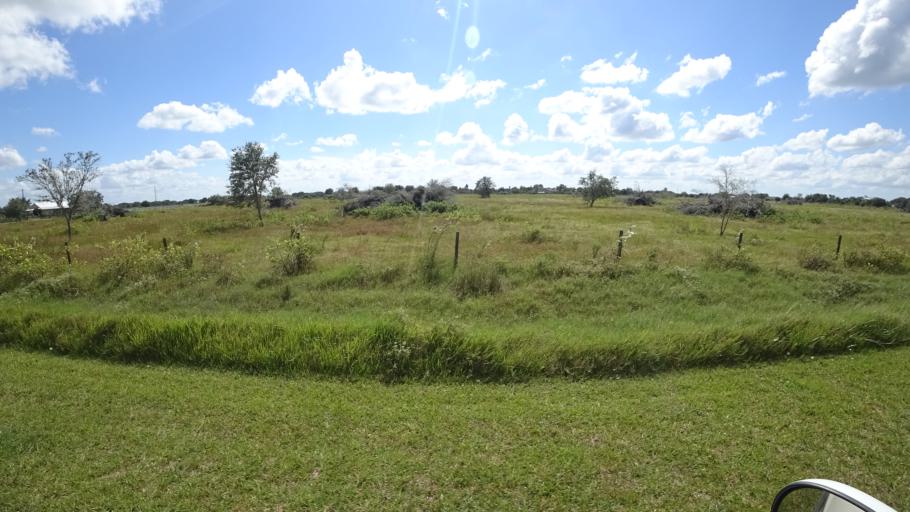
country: US
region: Florida
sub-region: Sarasota County
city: Warm Mineral Springs
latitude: 27.2858
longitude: -82.1942
